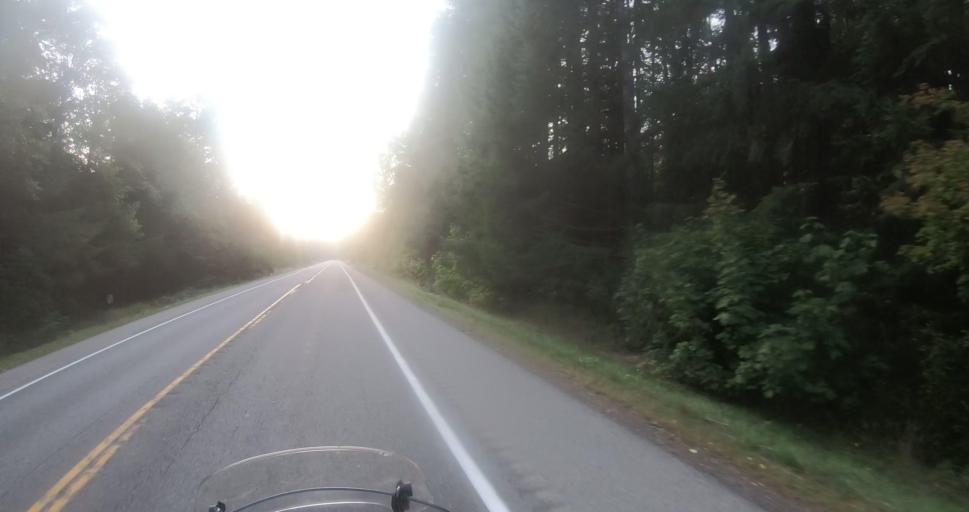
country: US
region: Washington
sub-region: Lewis County
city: Morton
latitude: 46.5389
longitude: -122.0304
